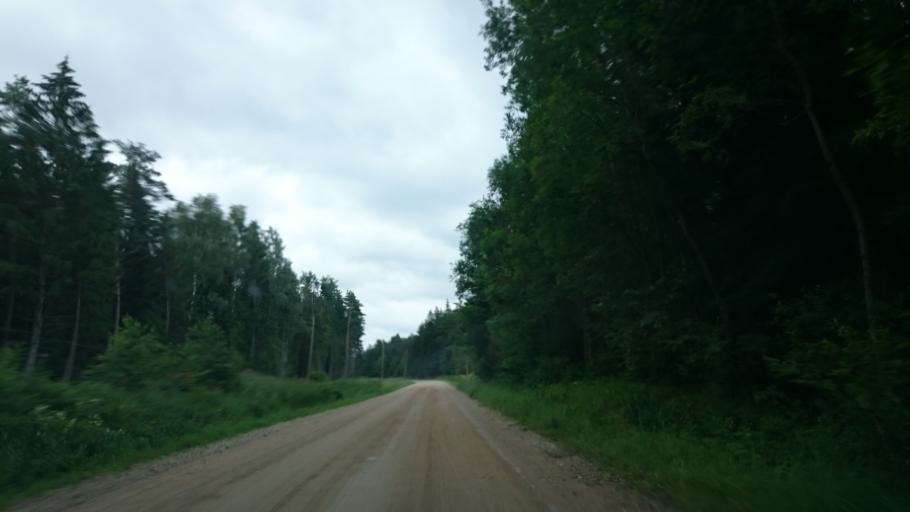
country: LV
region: Durbe
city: Liegi
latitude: 56.7553
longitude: 21.3370
